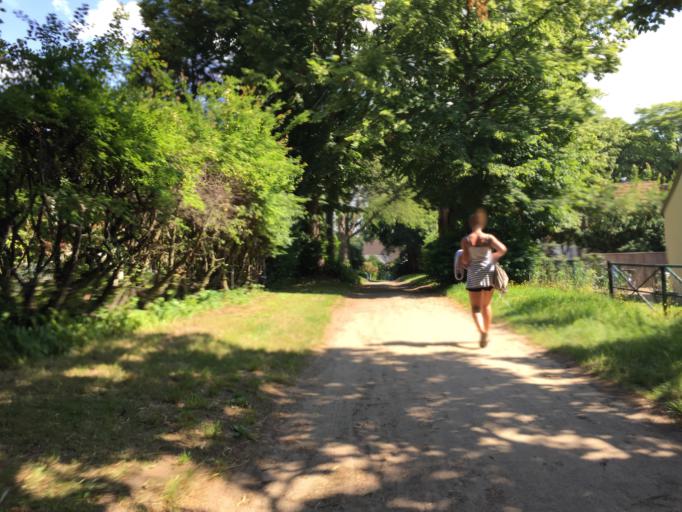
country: DE
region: Mecklenburg-Vorpommern
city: Hiddensee
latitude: 54.5864
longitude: 13.1058
